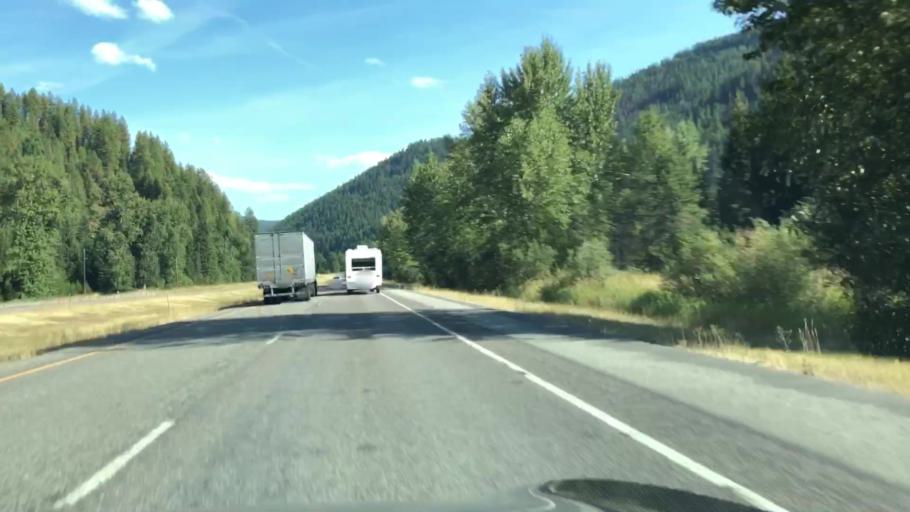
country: US
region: Montana
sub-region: Sanders County
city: Thompson Falls
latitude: 47.3633
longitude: -115.3245
